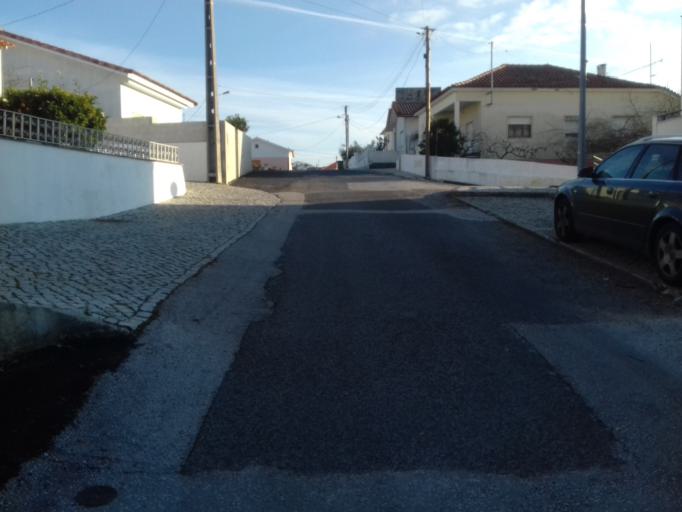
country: PT
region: Leiria
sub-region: Porto de Mos
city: Porto de Mos
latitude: 39.6024
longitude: -8.8137
